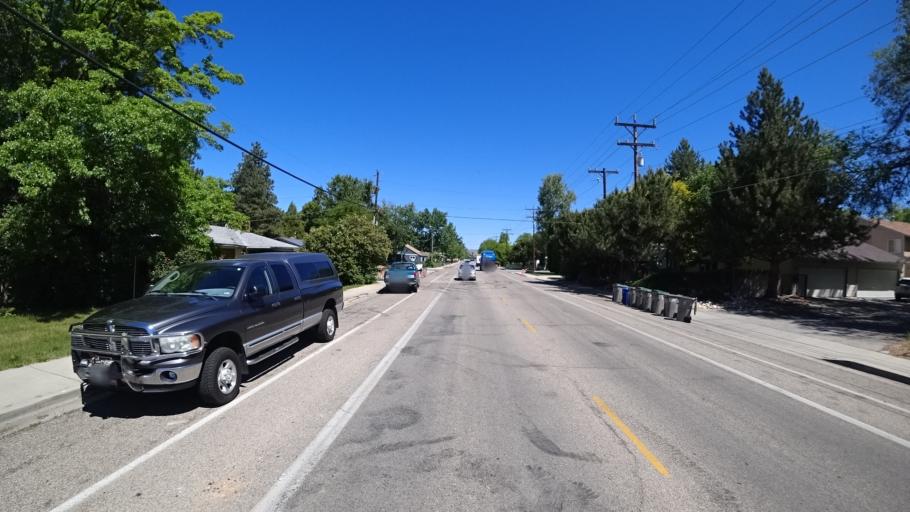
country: US
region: Idaho
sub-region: Ada County
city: Garden City
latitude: 43.5983
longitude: -116.2286
